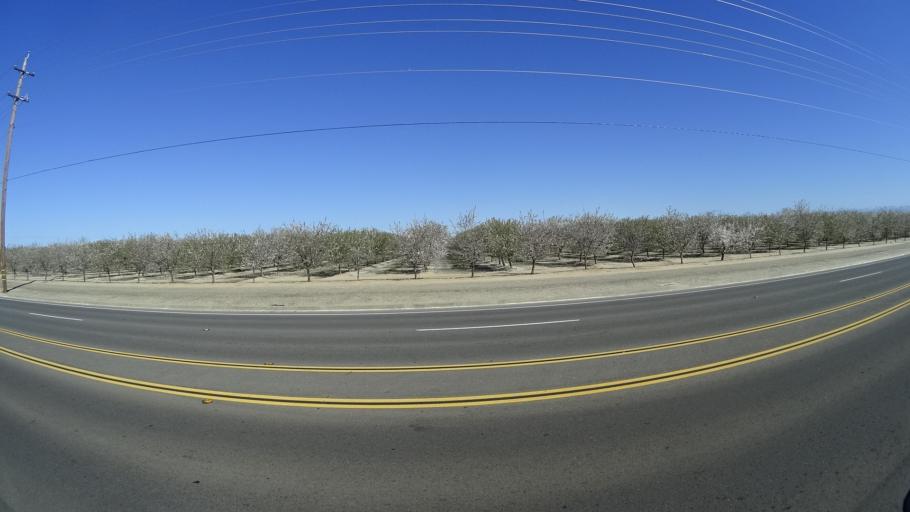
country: US
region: California
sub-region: Fresno County
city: Clovis
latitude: 36.8231
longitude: -119.7485
